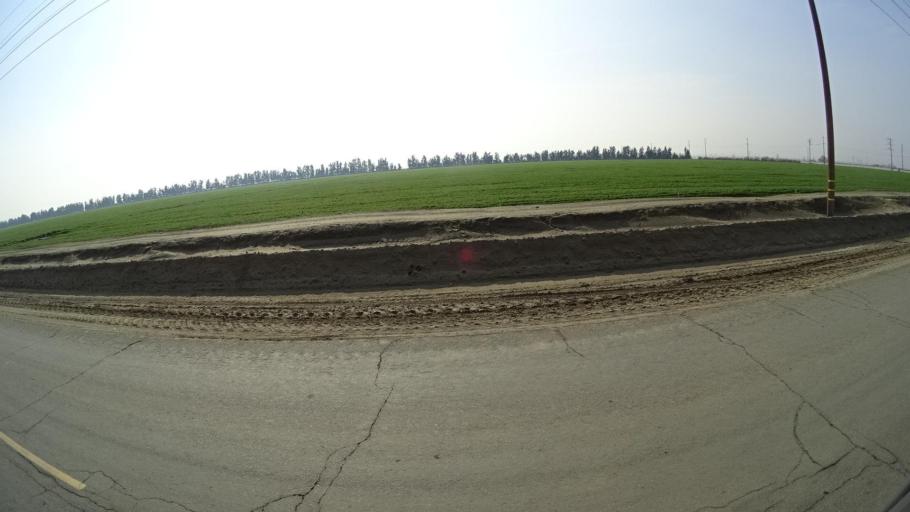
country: US
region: California
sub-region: Kern County
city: Arvin
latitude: 35.0929
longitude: -118.8751
